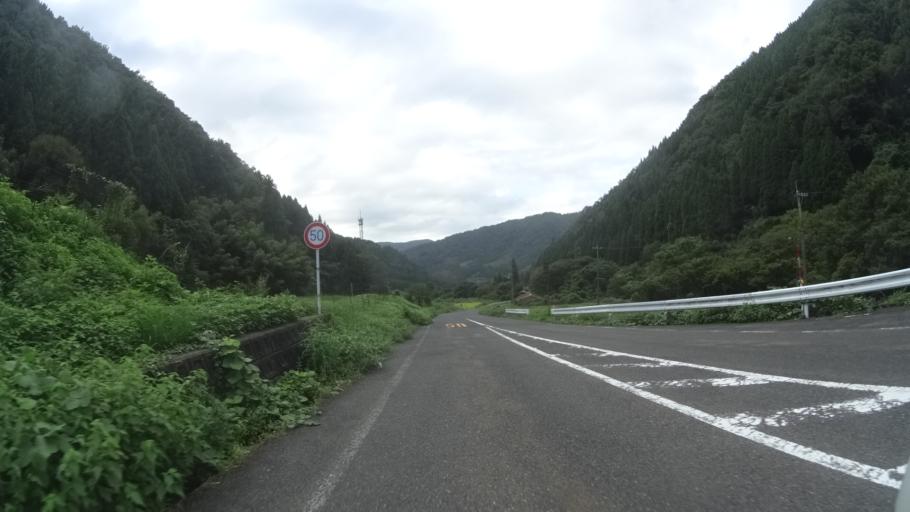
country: JP
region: Tottori
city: Kurayoshi
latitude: 35.4032
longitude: 133.9376
